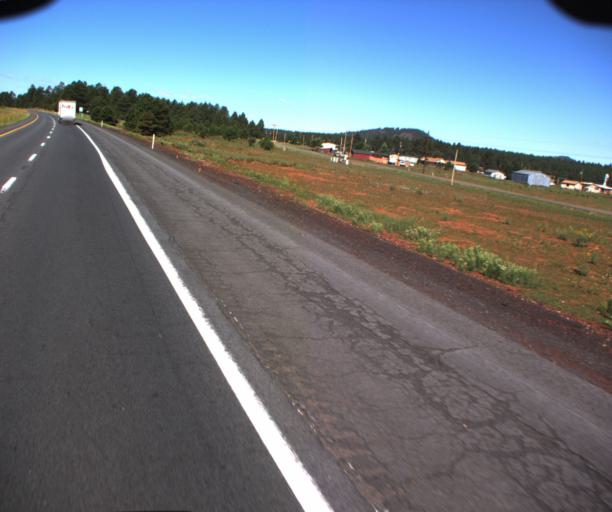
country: US
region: Arizona
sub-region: Coconino County
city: Parks
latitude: 35.2649
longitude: -112.0601
